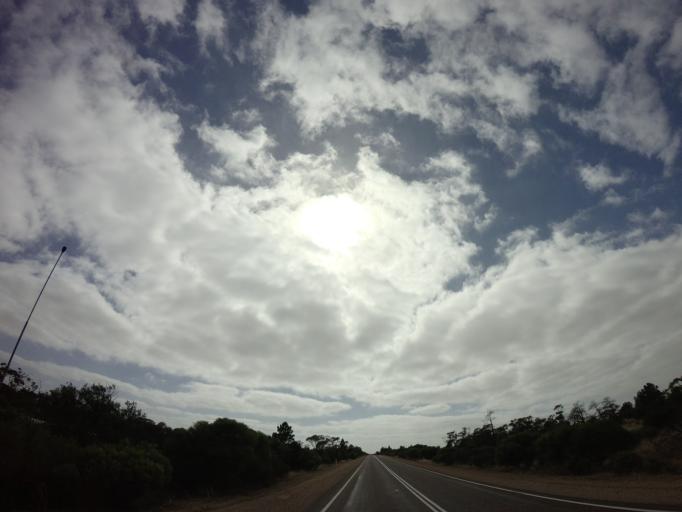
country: AU
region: South Australia
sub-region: Streaky Bay
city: Streaky Bay
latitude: -32.7234
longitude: 134.8445
